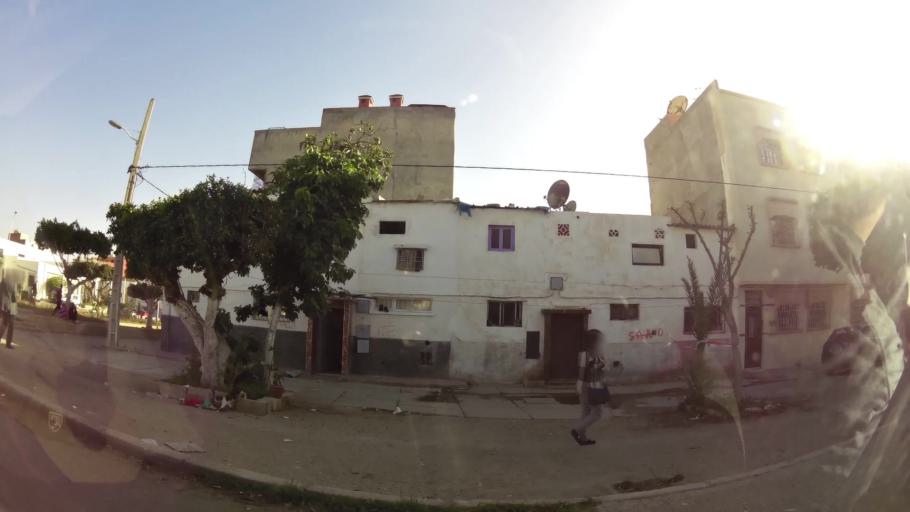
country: MA
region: Souss-Massa-Draa
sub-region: Agadir-Ida-ou-Tnan
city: Agadir
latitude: 30.4280
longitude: -9.5822
